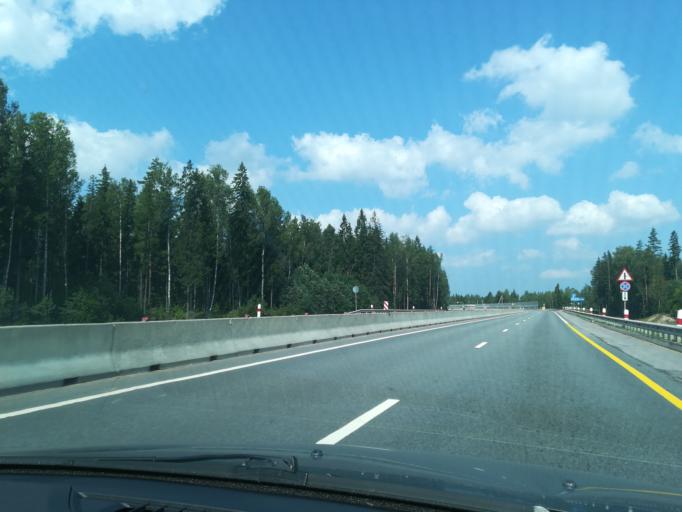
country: RU
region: Leningrad
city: Vistino
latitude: 59.6531
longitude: 28.5587
